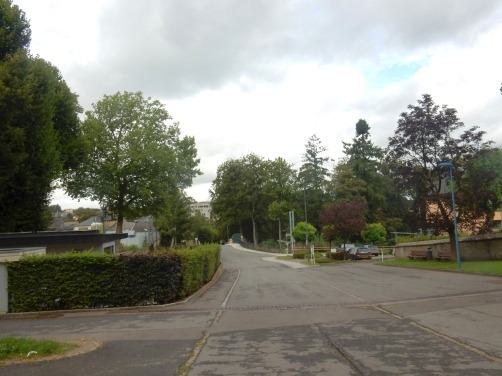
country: LU
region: Diekirch
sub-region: Canton de Diekirch
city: Ettelbruck
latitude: 49.8412
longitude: 6.1017
